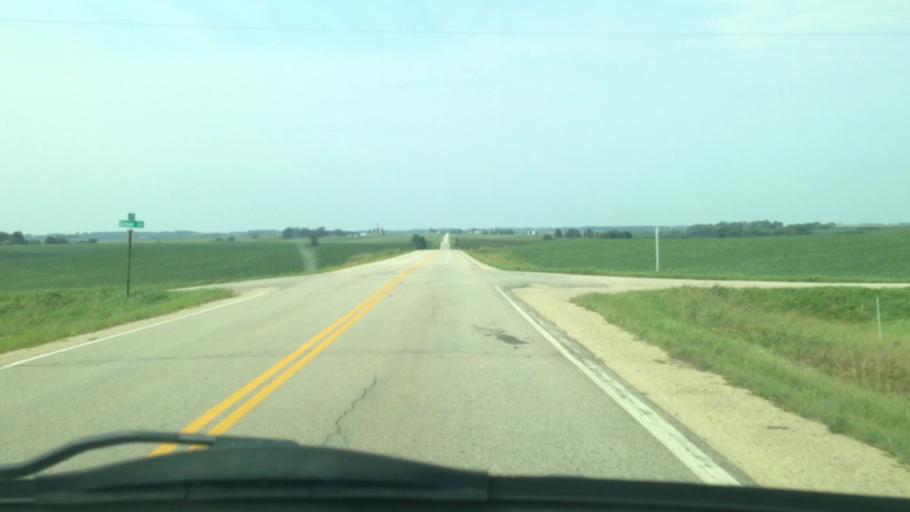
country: US
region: Minnesota
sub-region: Winona County
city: Saint Charles
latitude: 43.8611
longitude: -91.9593
